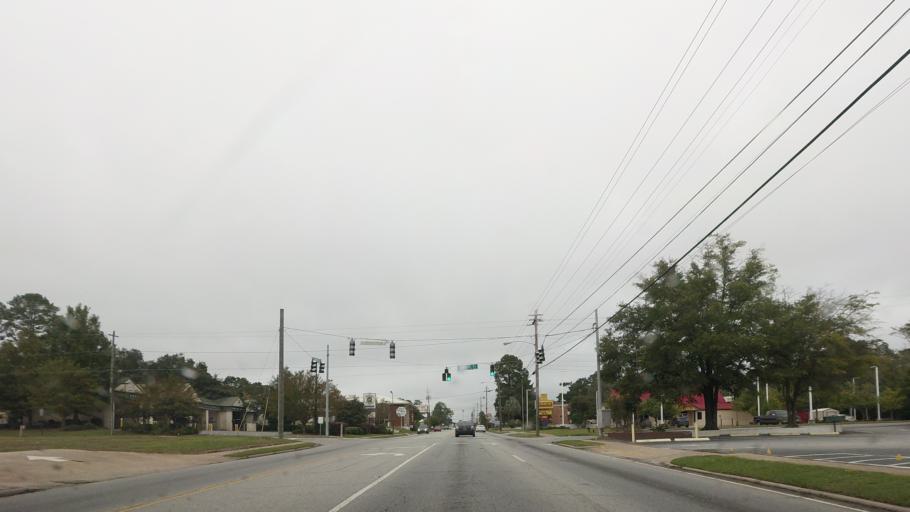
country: US
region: Georgia
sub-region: Lowndes County
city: Valdosta
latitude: 30.8524
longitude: -83.2807
